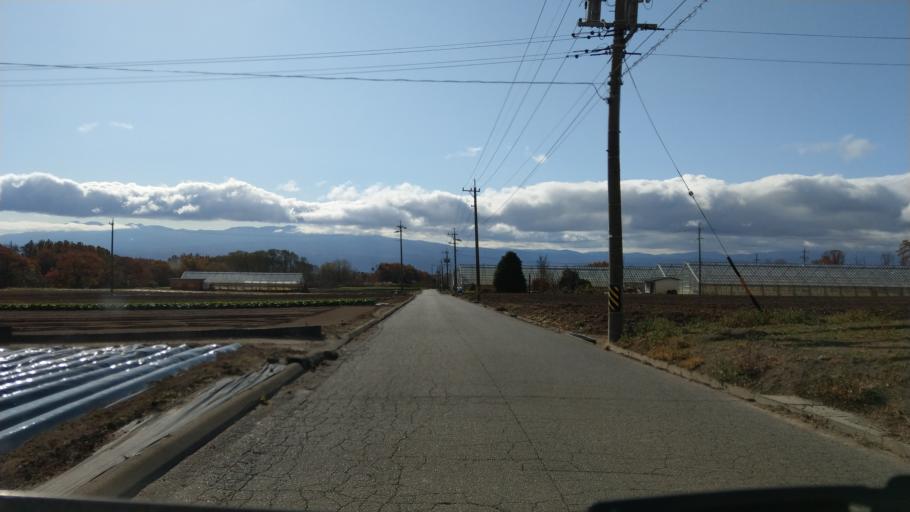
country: JP
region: Nagano
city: Komoro
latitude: 36.3182
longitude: 138.4836
